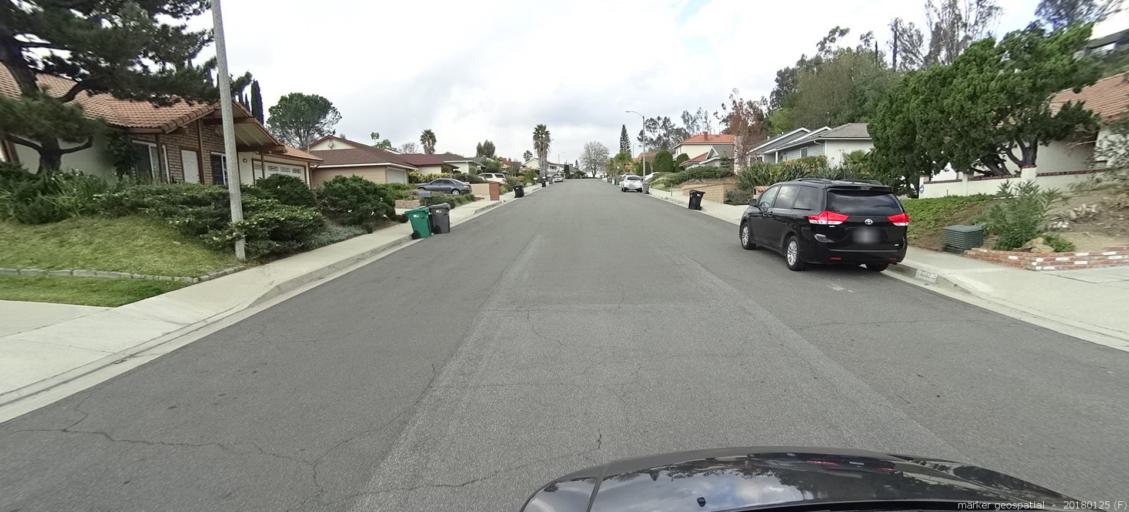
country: US
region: California
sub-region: Los Angeles County
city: Walnut
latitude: 33.9901
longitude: -117.8347
